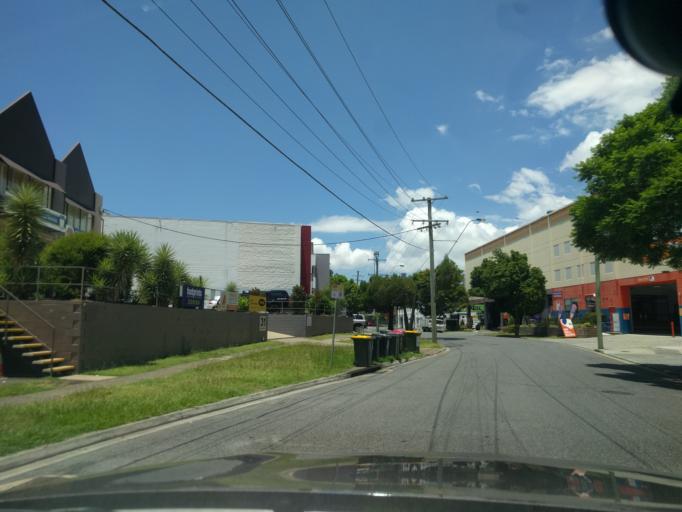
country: AU
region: Queensland
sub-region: Brisbane
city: Milton
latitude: -27.4670
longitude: 153.0068
